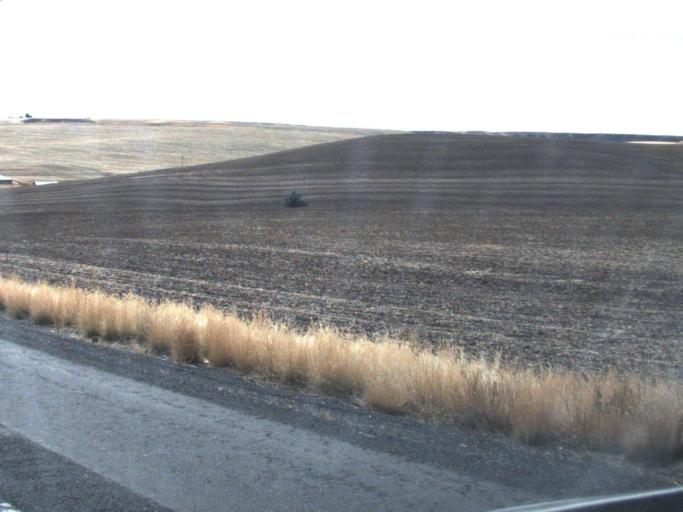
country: US
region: Washington
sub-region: Asotin County
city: Clarkston
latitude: 46.4776
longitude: -117.0523
